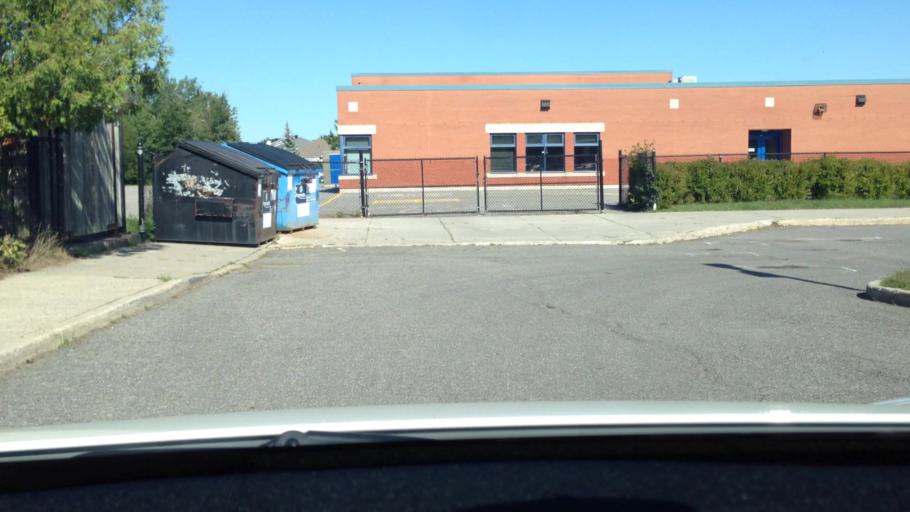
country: CA
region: Ontario
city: Clarence-Rockland
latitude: 45.4693
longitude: -75.4754
